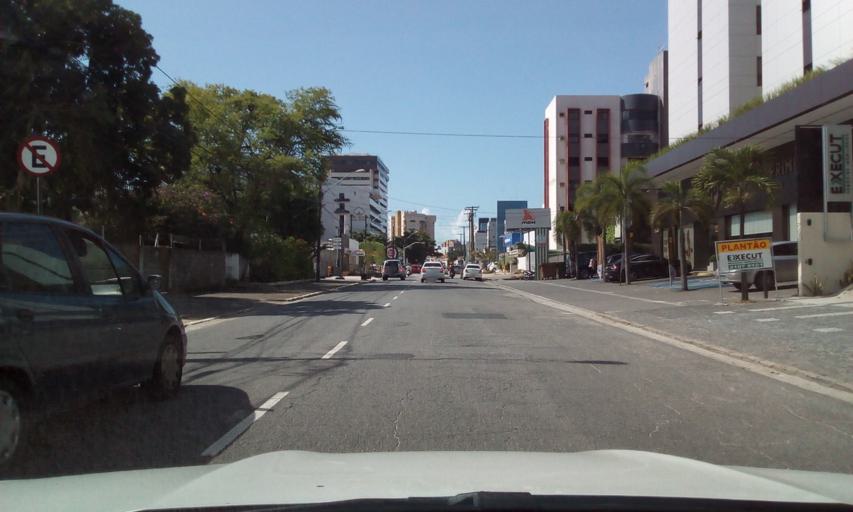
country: BR
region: Paraiba
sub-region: Joao Pessoa
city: Joao Pessoa
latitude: -7.1176
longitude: -34.8253
